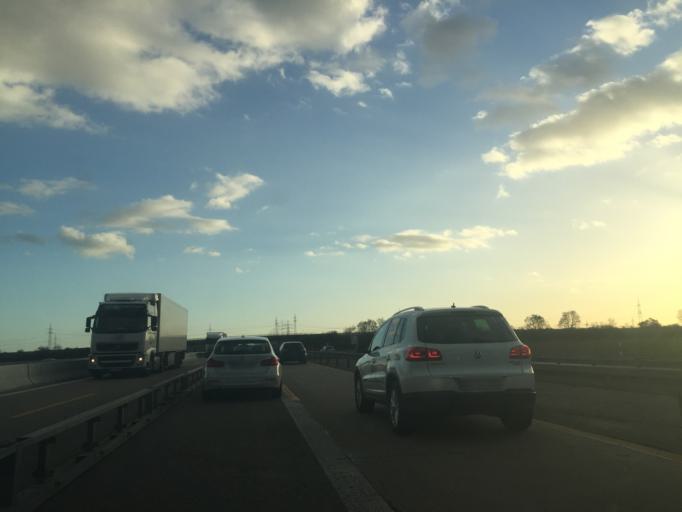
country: DE
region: Baden-Wuerttemberg
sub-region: Karlsruhe Region
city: Eppelheim
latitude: 49.3676
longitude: 8.6321
